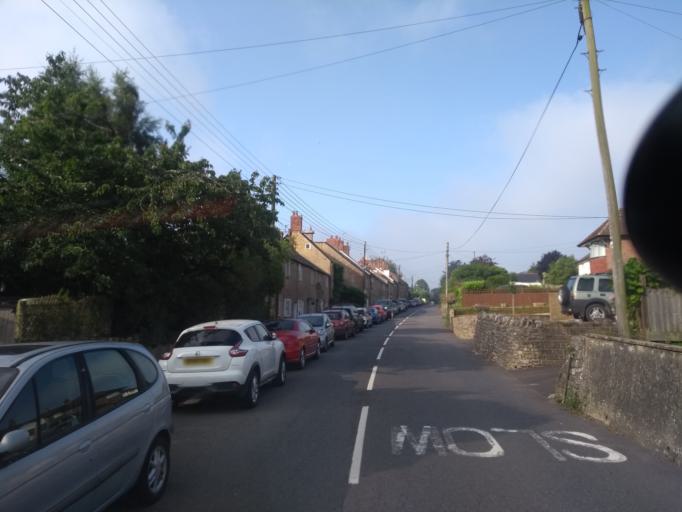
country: GB
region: England
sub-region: Somerset
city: Crewkerne
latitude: 50.8787
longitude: -2.7975
